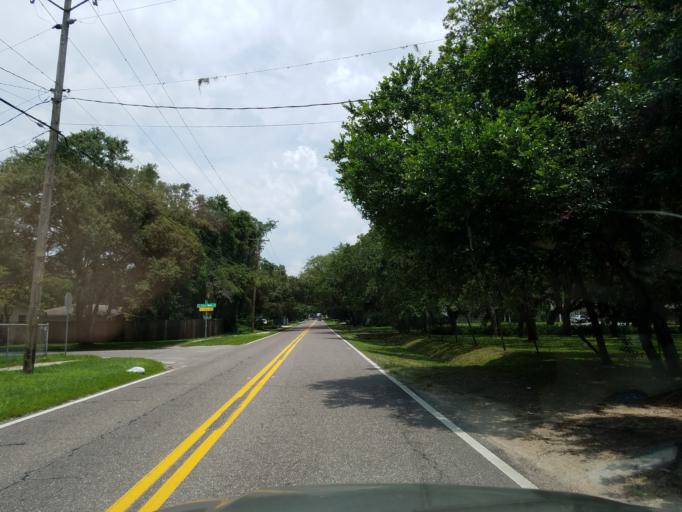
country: US
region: Florida
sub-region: Hillsborough County
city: Valrico
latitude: 27.9233
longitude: -82.2483
